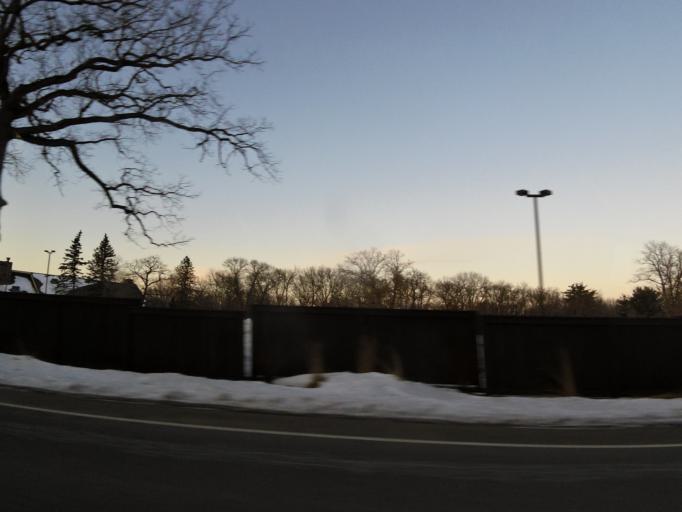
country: US
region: Minnesota
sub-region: Washington County
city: Dellwood
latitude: 45.0959
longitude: -92.9754
